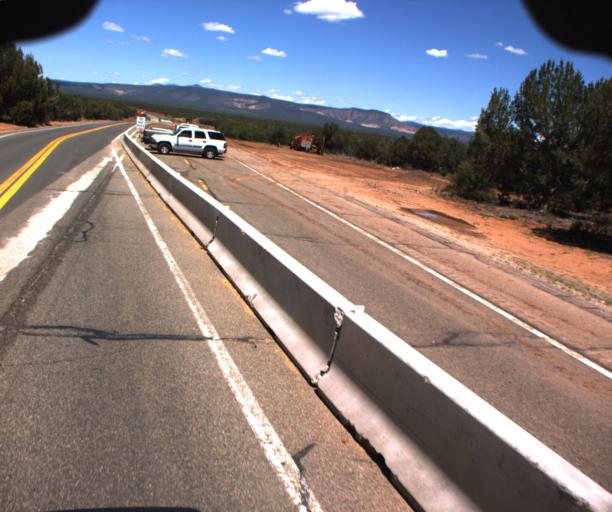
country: US
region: Arizona
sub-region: Yavapai County
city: Paulden
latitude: 34.9865
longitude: -112.3969
